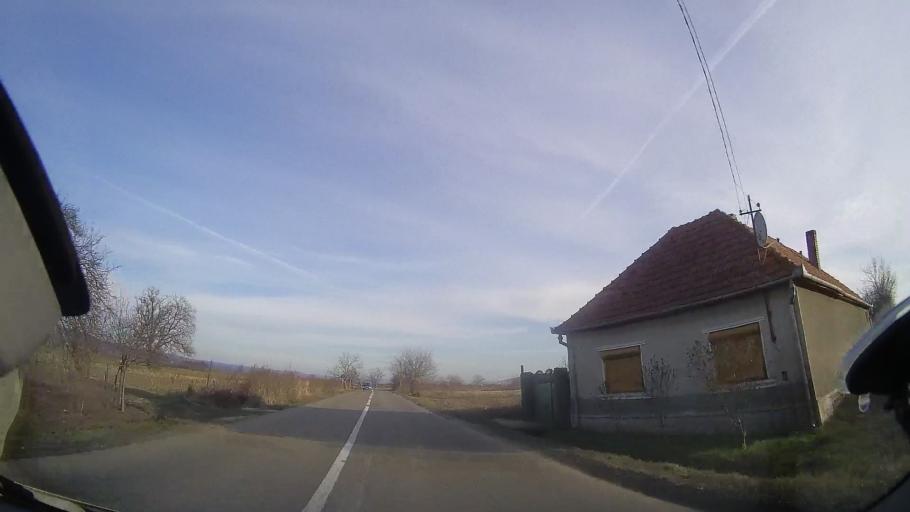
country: RO
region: Bihor
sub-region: Comuna Tileagd
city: Tileagd
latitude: 47.0594
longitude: 22.2453
